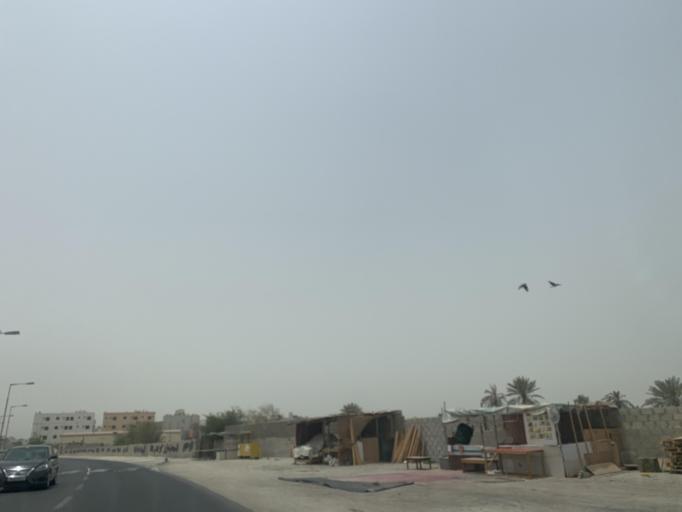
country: BH
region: Manama
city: Jidd Hafs
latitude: 26.2135
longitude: 50.5002
